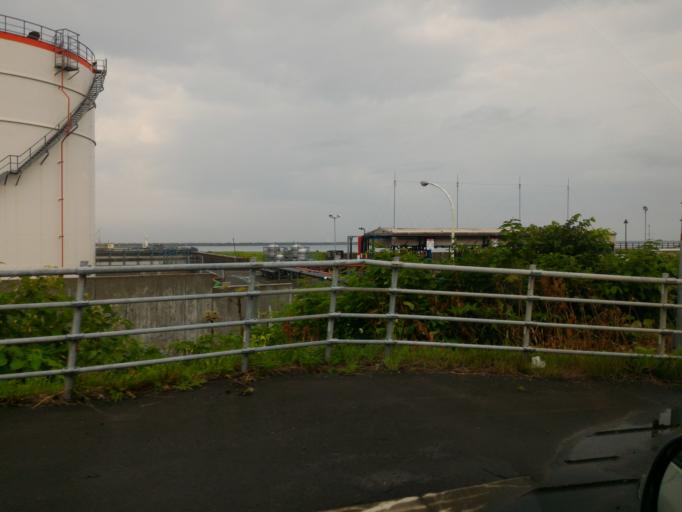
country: JP
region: Hokkaido
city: Rumoi
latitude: 43.9594
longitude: 141.6436
